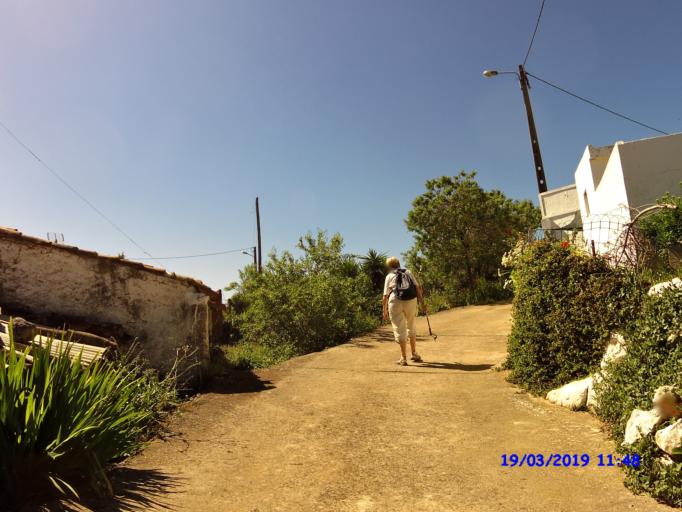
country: PT
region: Faro
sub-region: Loule
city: Boliqueime
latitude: 37.2100
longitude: -8.1464
